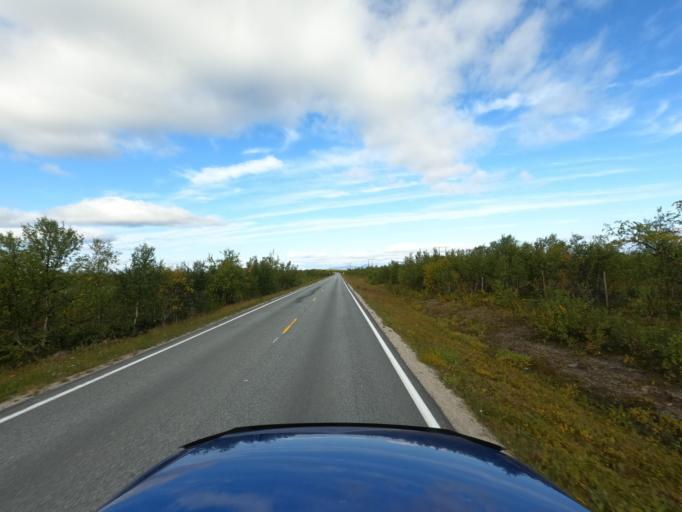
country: NO
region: Finnmark Fylke
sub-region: Karasjok
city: Karasjohka
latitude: 69.6597
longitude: 25.2770
